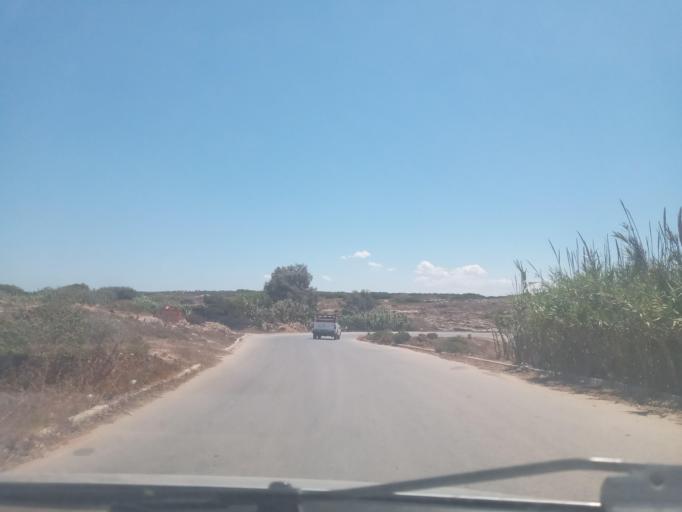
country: TN
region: Nabul
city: El Haouaria
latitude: 37.0524
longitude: 10.9897
